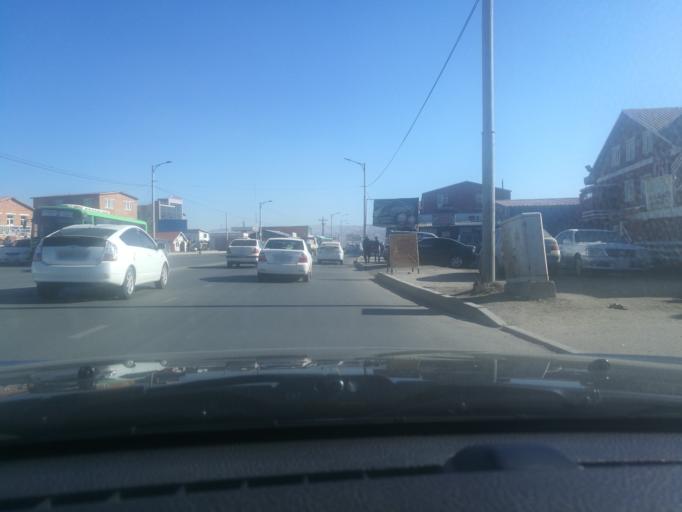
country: MN
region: Ulaanbaatar
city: Ulaanbaatar
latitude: 47.9393
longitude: 106.9112
